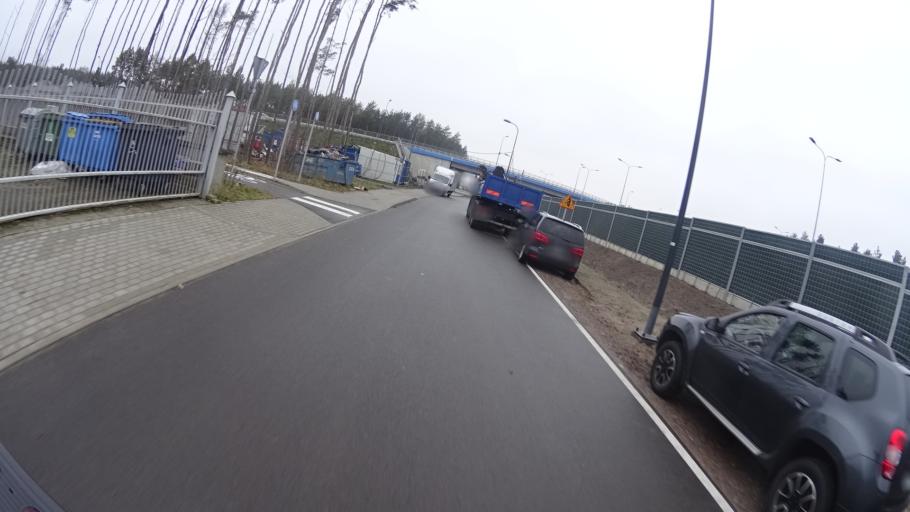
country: PL
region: Masovian Voivodeship
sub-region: Warszawa
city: Wawer
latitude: 52.1675
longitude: 21.1994
